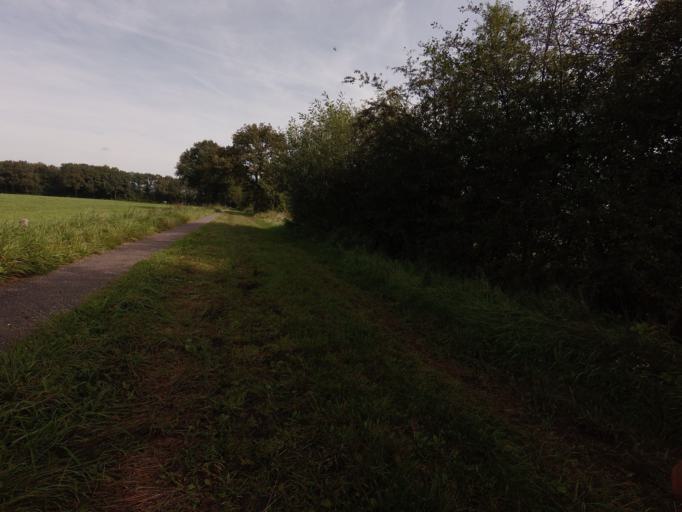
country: NL
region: Overijssel
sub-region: Gemeente Enschede
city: Enschede
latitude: 52.1841
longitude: 6.9403
